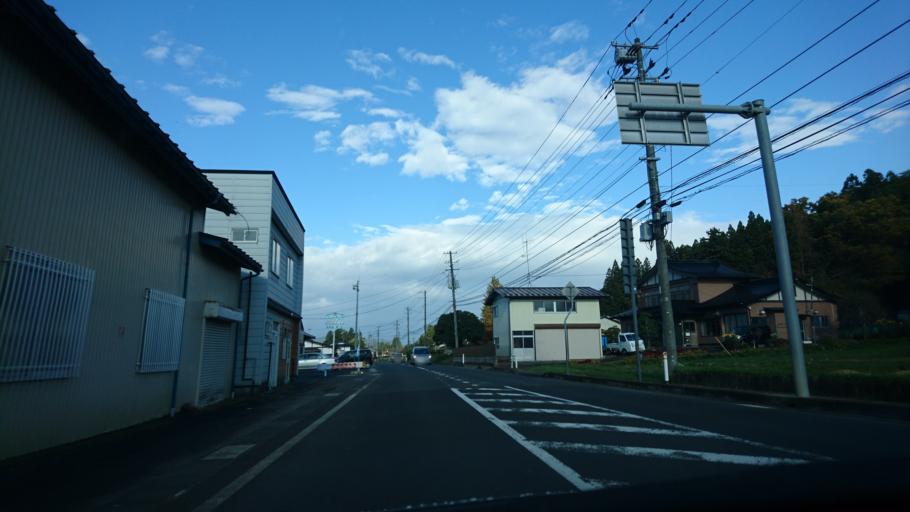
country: JP
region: Iwate
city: Ichinoseki
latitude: 39.0201
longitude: 141.0929
